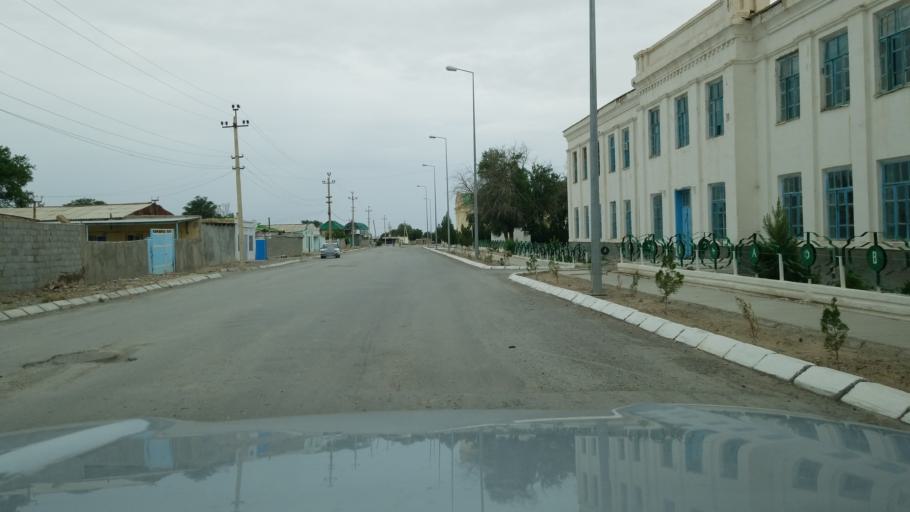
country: TM
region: Balkan
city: Serdar
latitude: 38.9845
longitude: 56.2754
